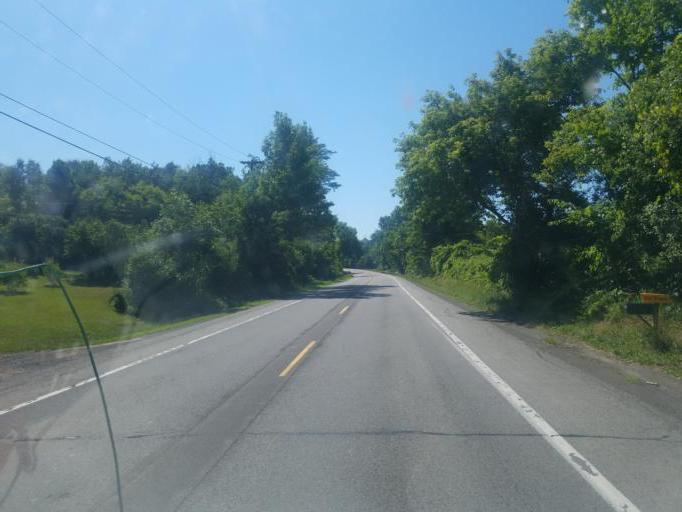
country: US
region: New York
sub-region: Ontario County
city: Phelps
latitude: 42.9504
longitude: -77.0279
